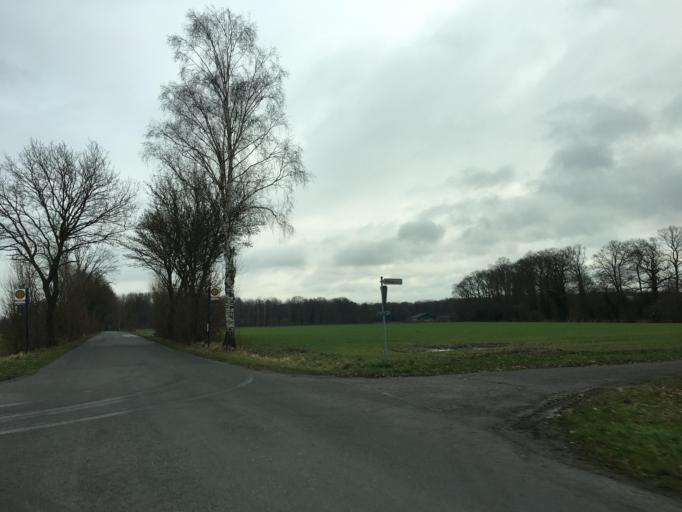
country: DE
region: North Rhine-Westphalia
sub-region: Regierungsbezirk Munster
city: Senden
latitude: 51.8808
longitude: 7.4651
